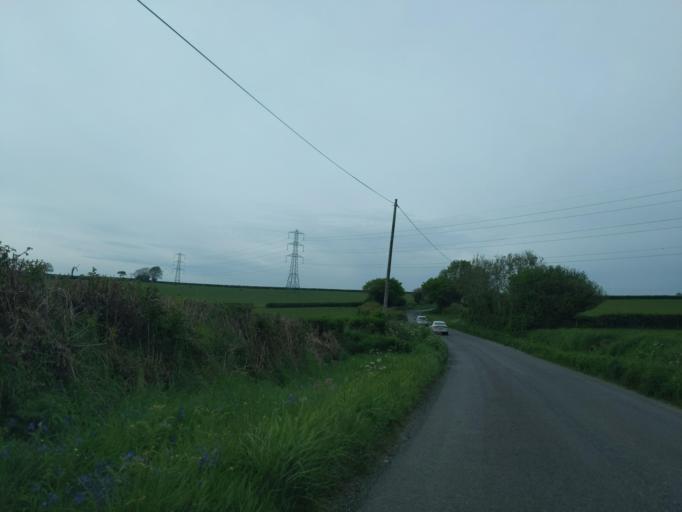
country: GB
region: England
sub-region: Devon
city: Plympton
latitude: 50.4254
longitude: -4.0484
